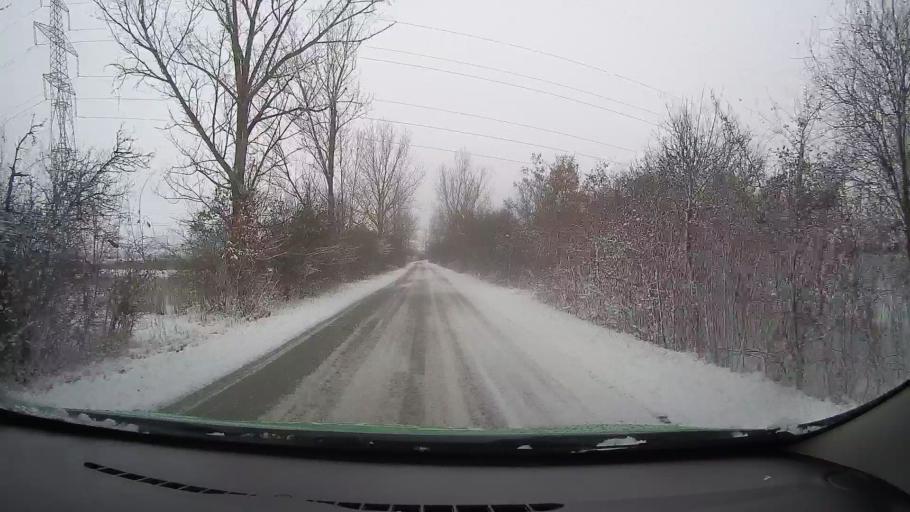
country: RO
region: Hunedoara
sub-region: Municipiul Hunedoara
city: Pestisu Mare
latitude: 45.8081
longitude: 22.9118
